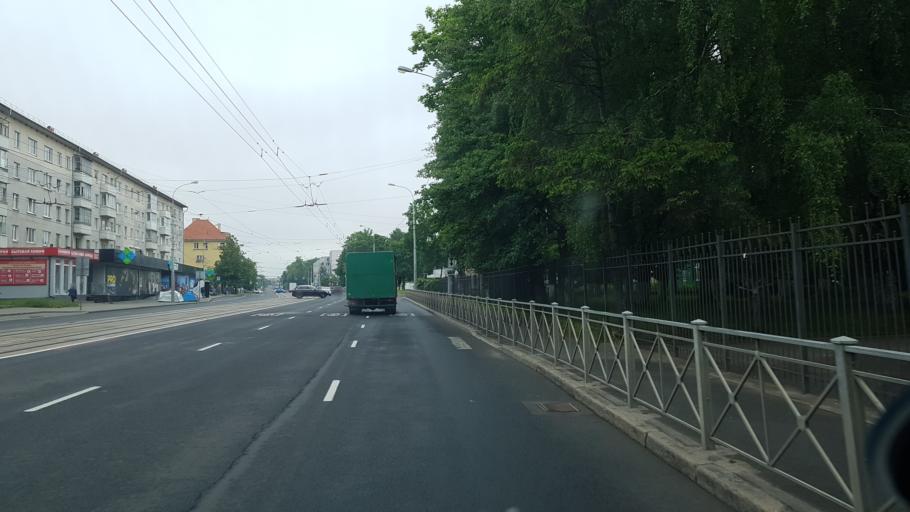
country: RU
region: Kaliningrad
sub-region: Gorod Kaliningrad
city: Kaliningrad
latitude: 54.7285
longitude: 20.4928
